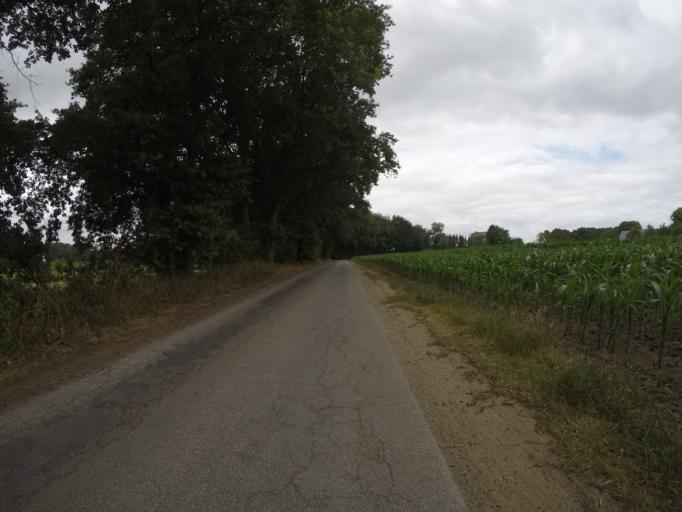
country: DE
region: North Rhine-Westphalia
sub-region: Regierungsbezirk Dusseldorf
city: Hamminkeln
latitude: 51.7685
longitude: 6.5942
